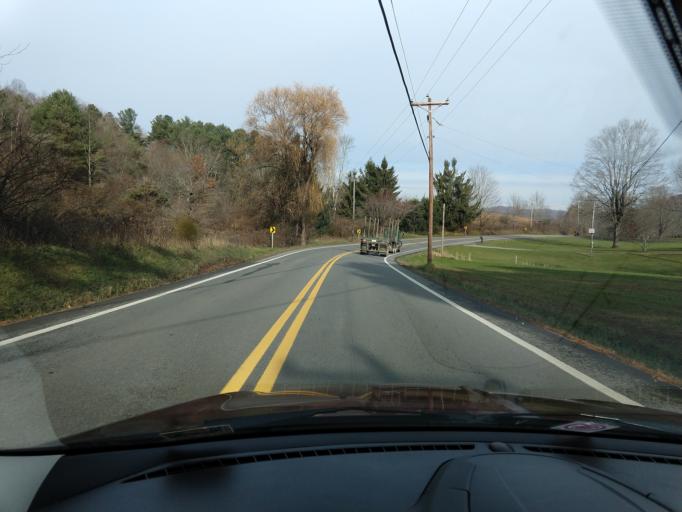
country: US
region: West Virginia
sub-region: Greenbrier County
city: Rainelle
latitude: 37.9371
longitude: -80.6517
